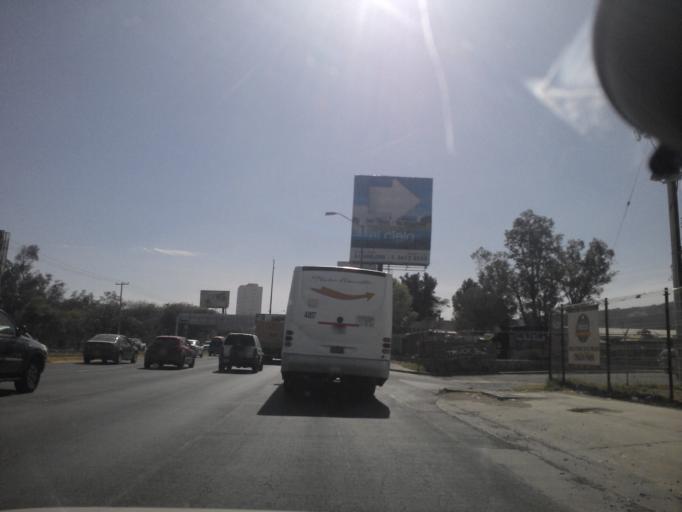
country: MX
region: Jalisco
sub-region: Tlajomulco de Zuniga
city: La Tijera
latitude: 20.5936
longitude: -103.4410
